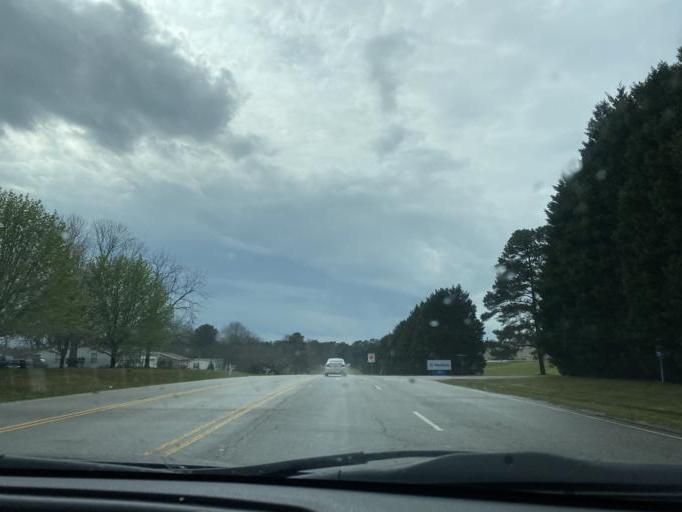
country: US
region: South Carolina
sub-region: Spartanburg County
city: Cowpens
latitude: 35.0179
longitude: -81.7772
